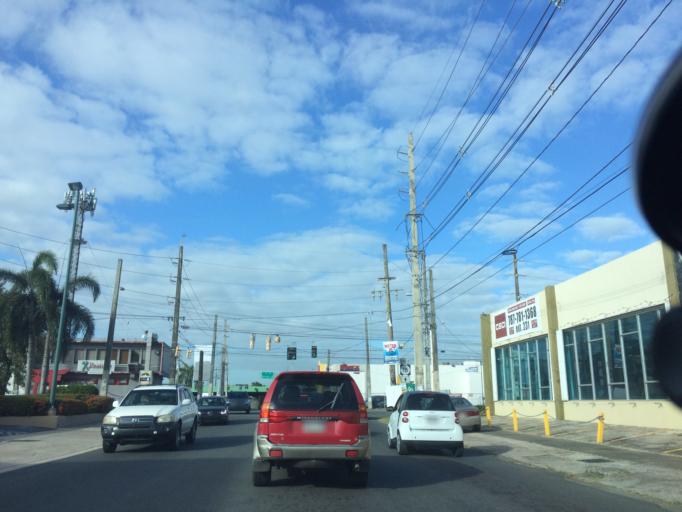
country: PR
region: Catano
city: Catano
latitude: 18.4267
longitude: -66.0711
